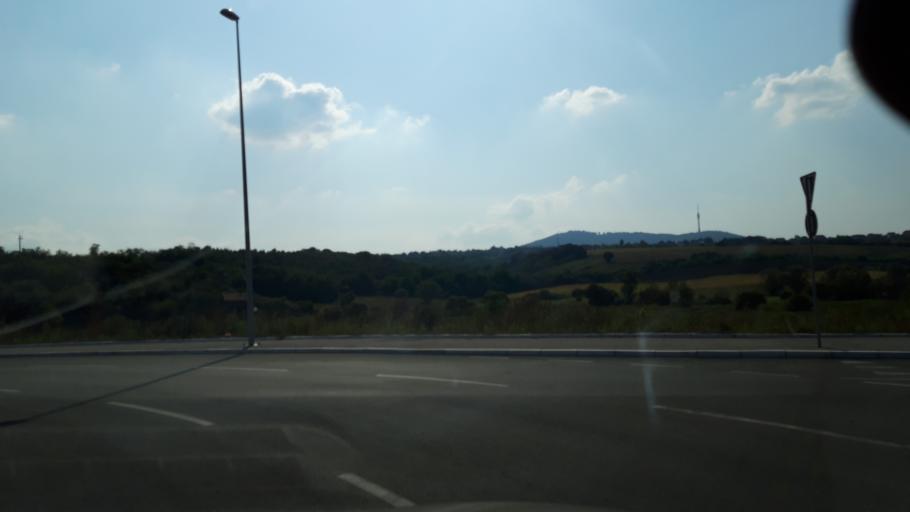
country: RS
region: Central Serbia
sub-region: Belgrade
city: Zvezdara
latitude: 44.7030
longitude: 20.5730
